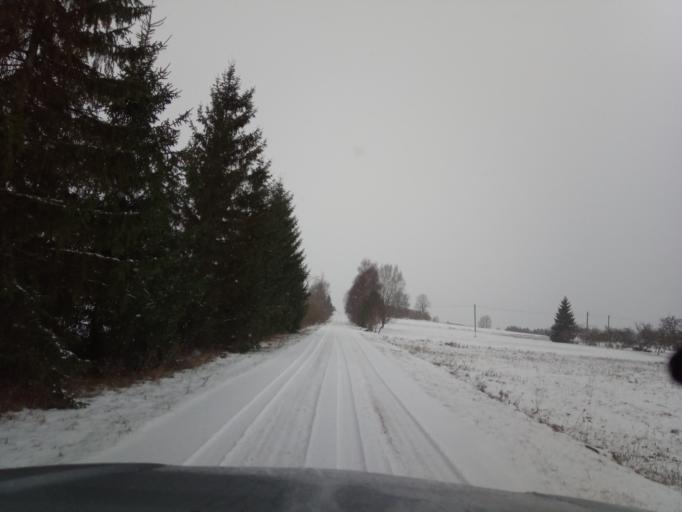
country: LT
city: Ramygala
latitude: 55.5899
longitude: 24.3501
